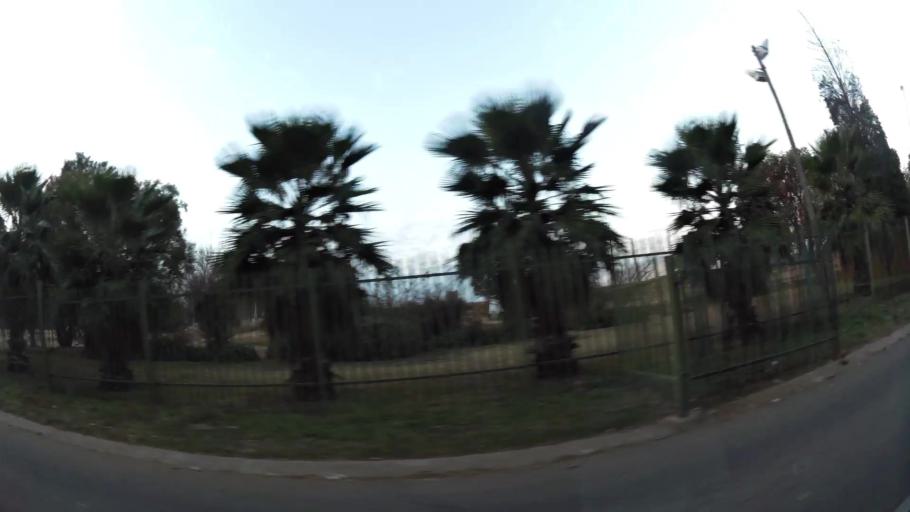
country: ZA
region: Gauteng
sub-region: City of Johannesburg Metropolitan Municipality
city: Diepsloot
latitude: -26.0014
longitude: 28.0434
